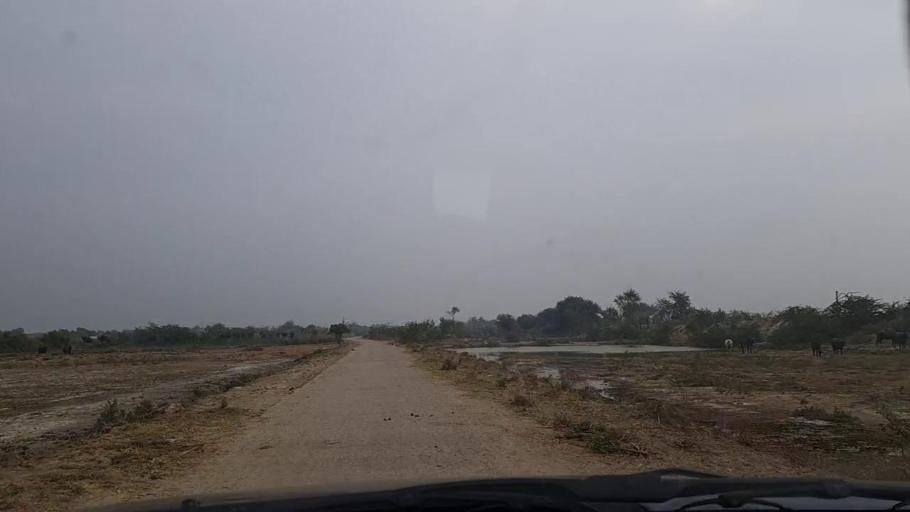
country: PK
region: Sindh
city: Tando Mittha Khan
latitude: 25.8060
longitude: 69.3763
